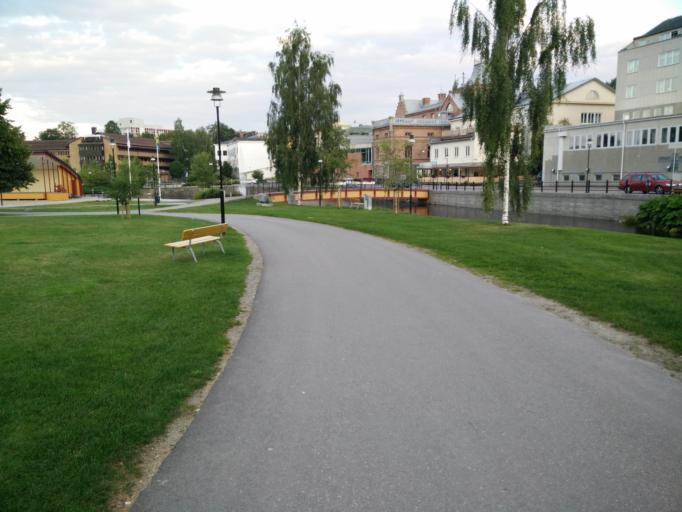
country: SE
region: Vaesternorrland
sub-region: Solleftea Kommun
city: Solleftea
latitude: 63.1683
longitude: 17.2690
